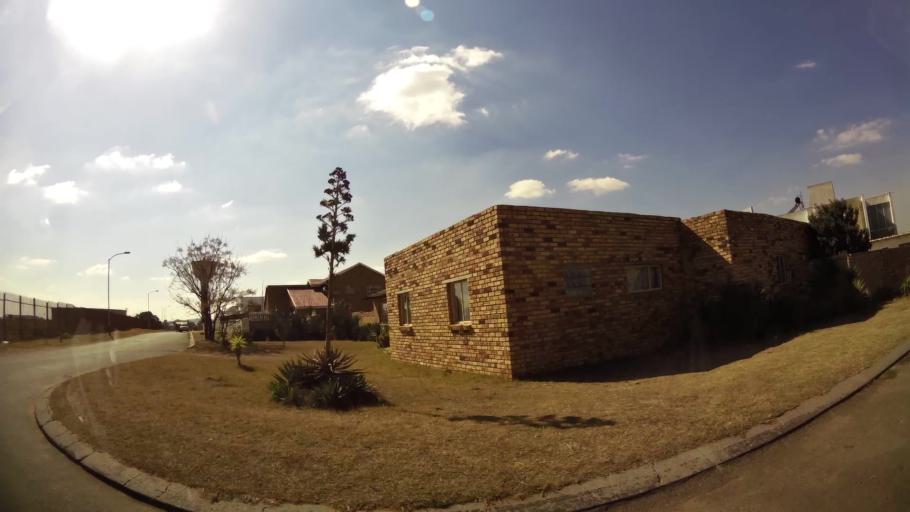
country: ZA
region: Gauteng
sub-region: West Rand District Municipality
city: Randfontein
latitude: -26.1656
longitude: 27.7504
